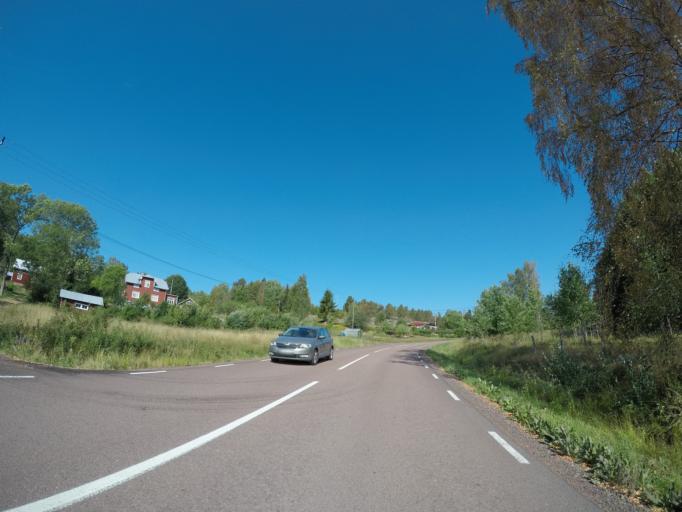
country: AX
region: Alands landsbygd
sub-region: Finstroem
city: Finstroem
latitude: 60.2725
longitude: 19.9217
